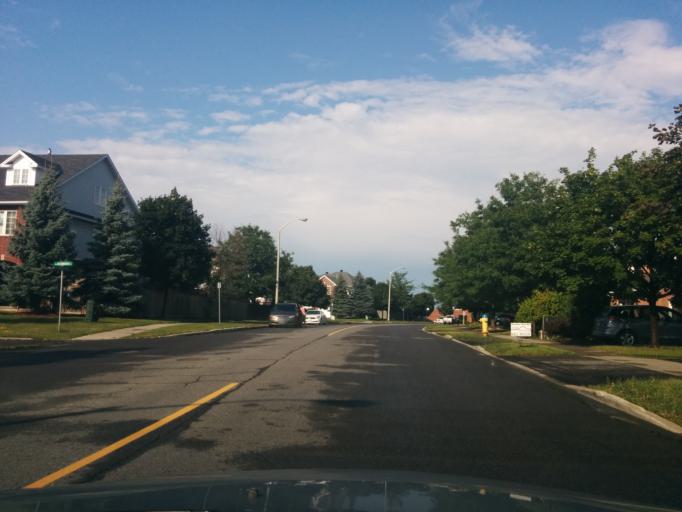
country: CA
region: Ontario
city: Ottawa
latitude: 45.3696
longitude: -75.7348
